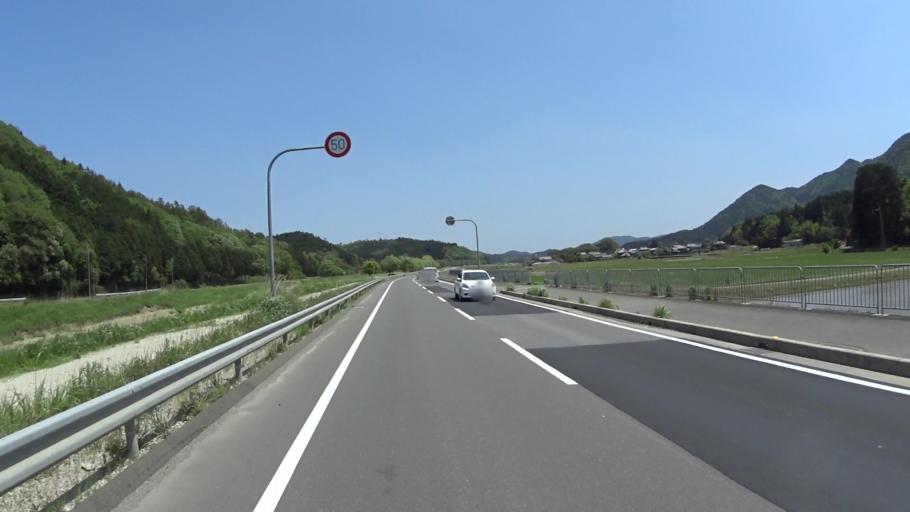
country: JP
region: Kyoto
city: Kameoka
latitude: 35.0613
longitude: 135.4576
